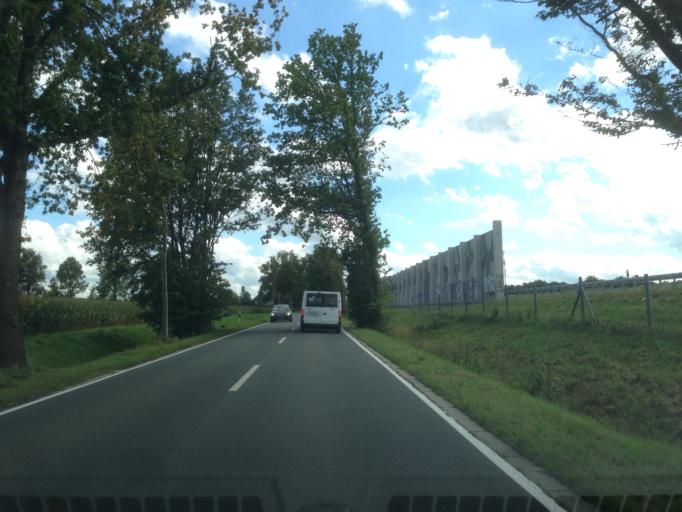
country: DE
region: North Rhine-Westphalia
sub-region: Regierungsbezirk Munster
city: Muenster
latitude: 51.8987
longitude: 7.5703
